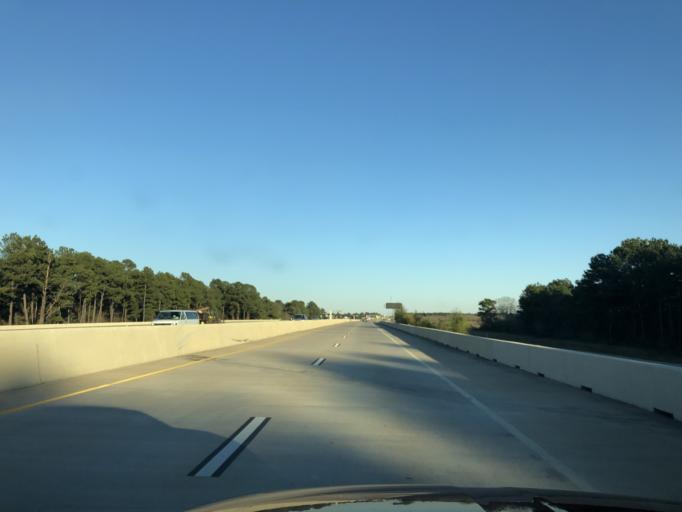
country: US
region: Texas
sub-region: Harris County
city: Tomball
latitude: 30.0508
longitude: -95.6559
